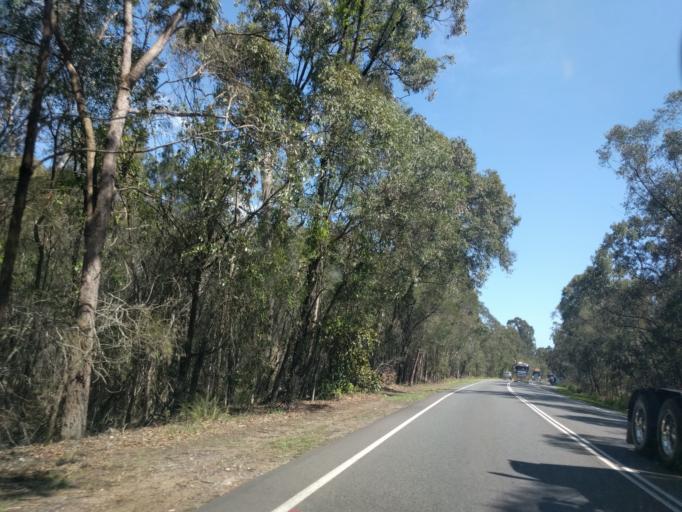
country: AU
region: Queensland
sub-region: Brisbane
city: Forest Lake
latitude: -27.6441
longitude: 152.9762
